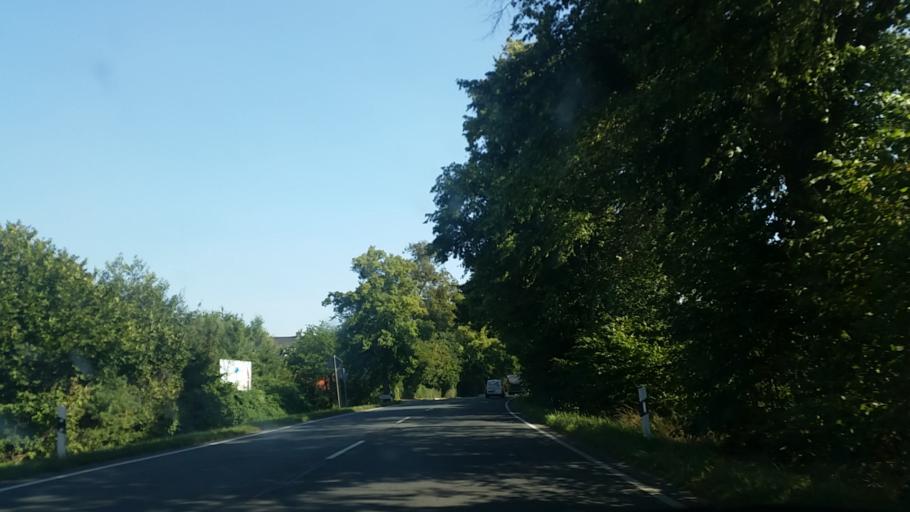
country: DE
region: Lower Saxony
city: Coppenbrugge
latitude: 52.1016
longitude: 9.5796
